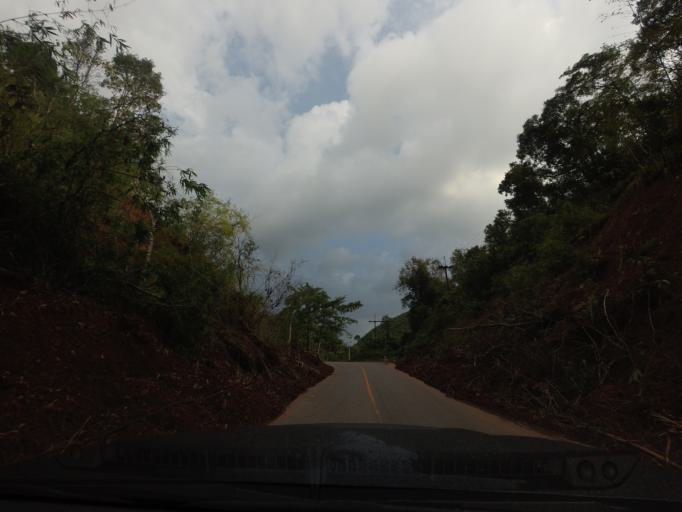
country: TH
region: Nan
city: Bo Kluea
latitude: 19.2636
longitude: 101.1786
